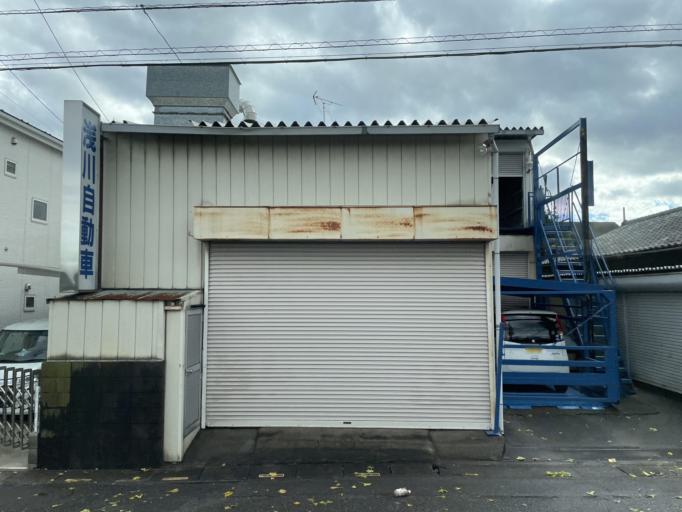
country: JP
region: Saitama
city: Koshigaya
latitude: 35.9087
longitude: 139.7944
